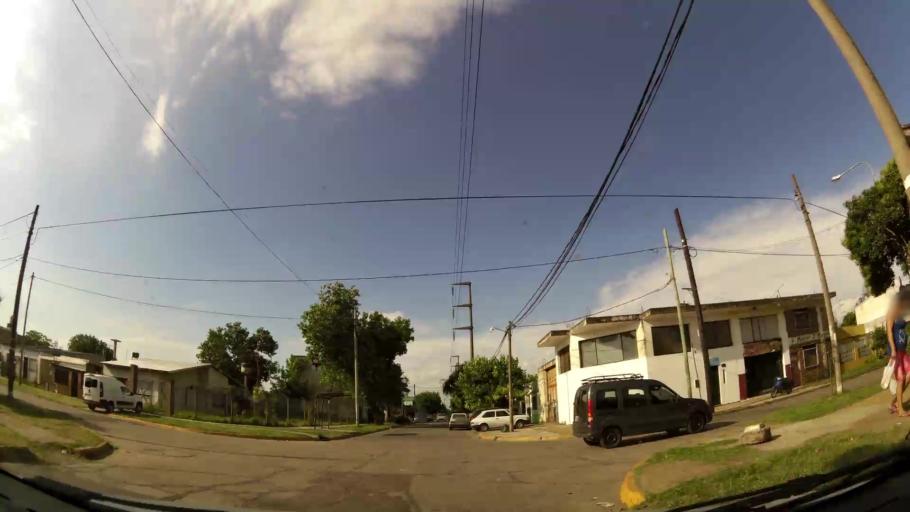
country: AR
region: Buenos Aires
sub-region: Partido de Merlo
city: Merlo
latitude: -34.6594
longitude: -58.7357
